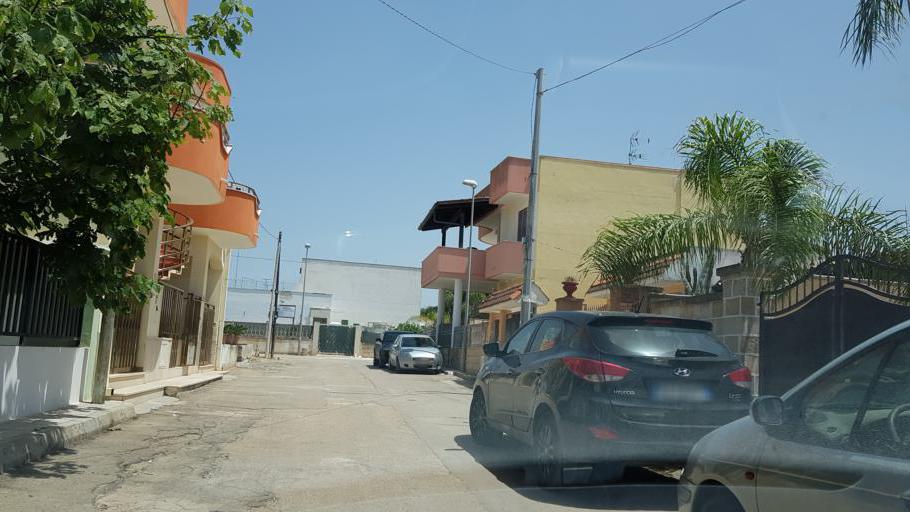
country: IT
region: Apulia
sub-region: Provincia di Lecce
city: Porto Cesareo
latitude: 40.2365
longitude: 17.9132
